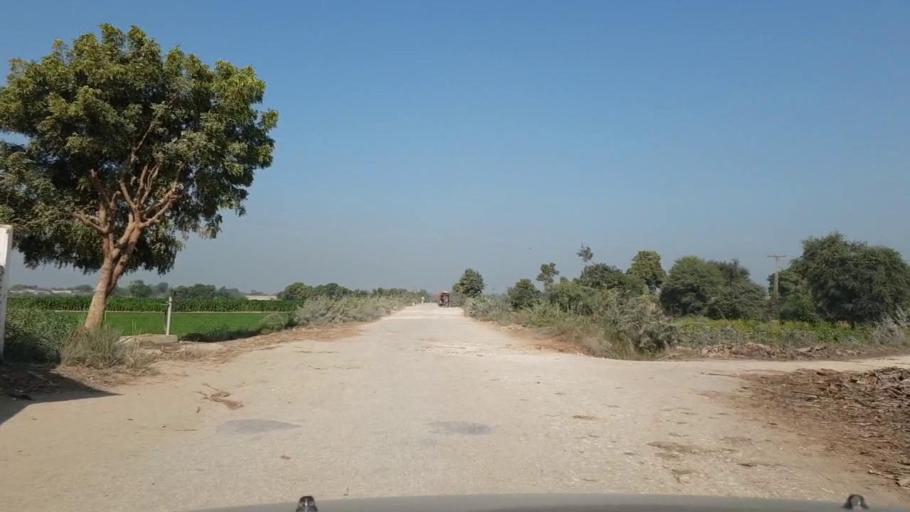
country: PK
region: Sindh
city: Matiari
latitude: 25.5781
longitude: 68.6045
